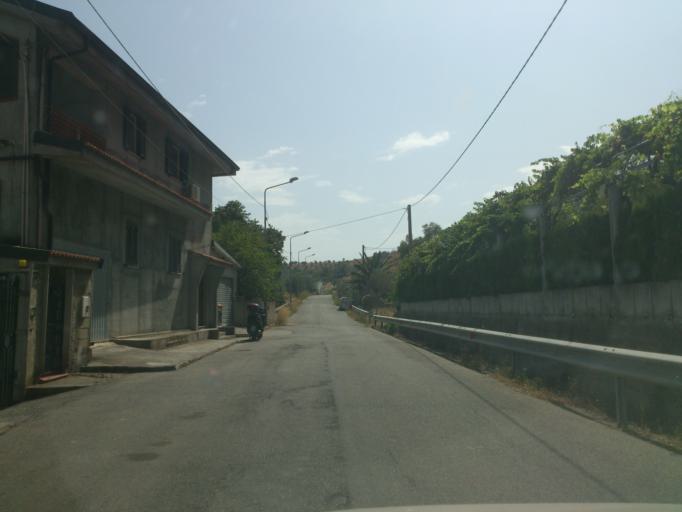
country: IT
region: Calabria
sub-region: Provincia di Reggio Calabria
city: Pazzano
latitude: 38.4678
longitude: 16.4551
